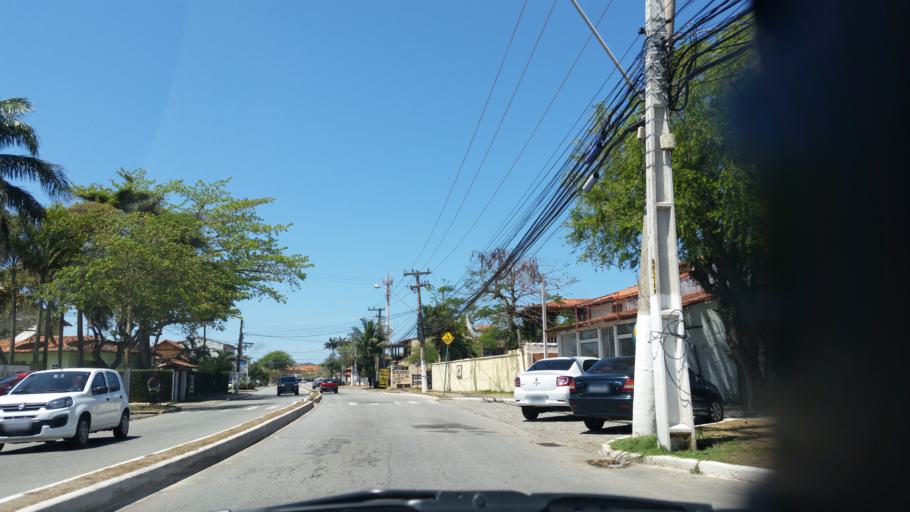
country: BR
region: Rio de Janeiro
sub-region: Armacao De Buzios
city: Armacao de Buzios
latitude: -22.7748
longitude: -41.9177
